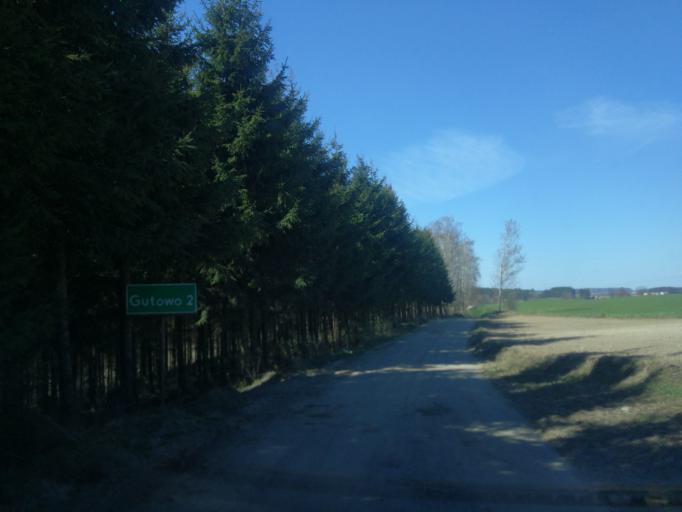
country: PL
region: Warmian-Masurian Voivodeship
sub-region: Powiat dzialdowski
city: Rybno
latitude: 53.4381
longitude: 19.9546
